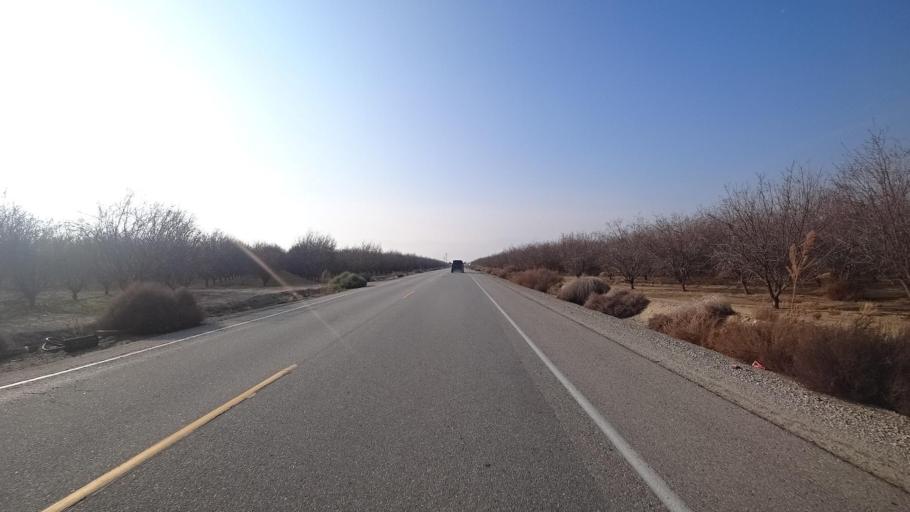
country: US
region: California
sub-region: Kern County
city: Lebec
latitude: 35.0275
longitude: -118.9287
